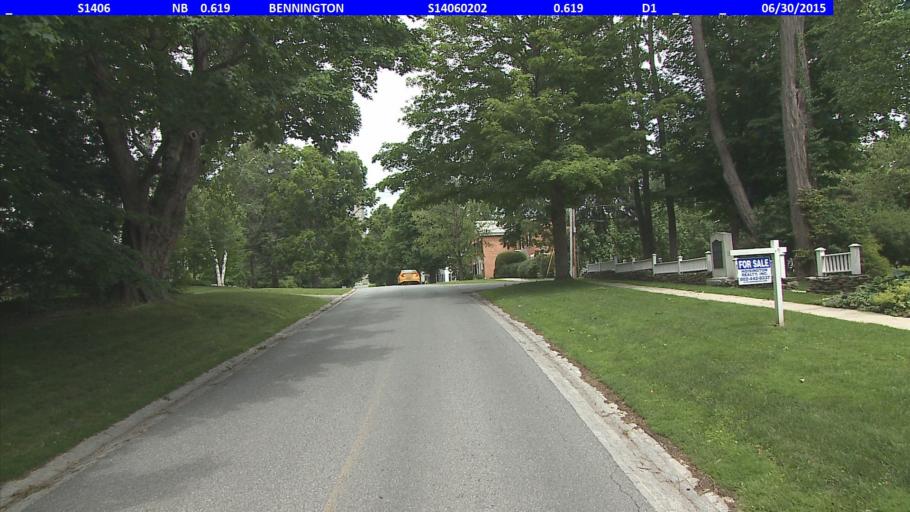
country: US
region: Vermont
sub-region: Bennington County
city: Bennington
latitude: 42.8859
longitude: -73.2139
